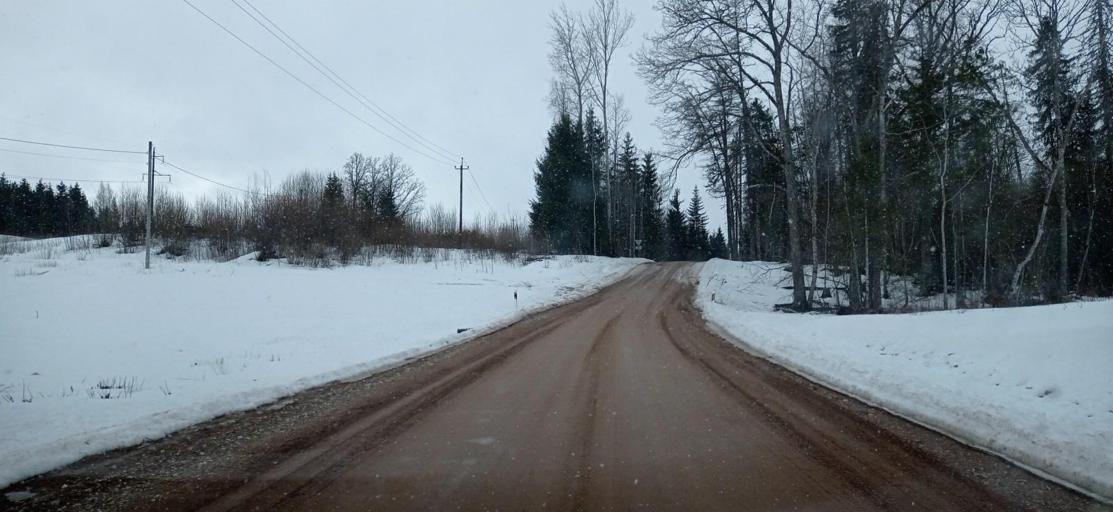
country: EE
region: Tartu
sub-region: UElenurme vald
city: Ulenurme
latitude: 58.1235
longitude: 26.7008
